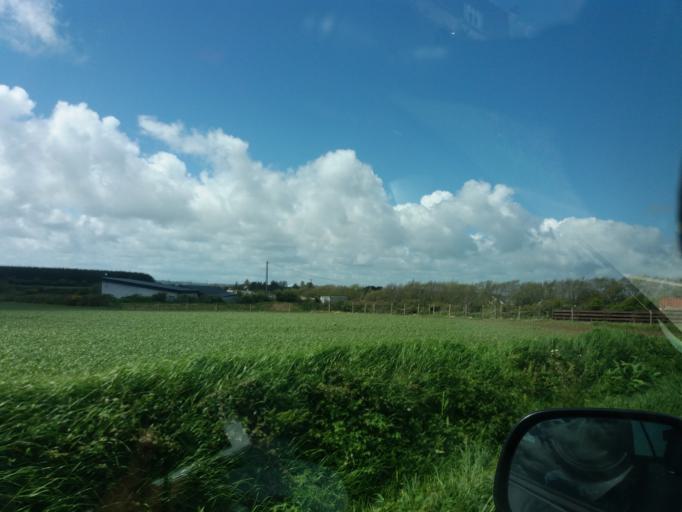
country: IE
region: Munster
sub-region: Waterford
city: Dunmore East
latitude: 52.2079
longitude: -6.8975
